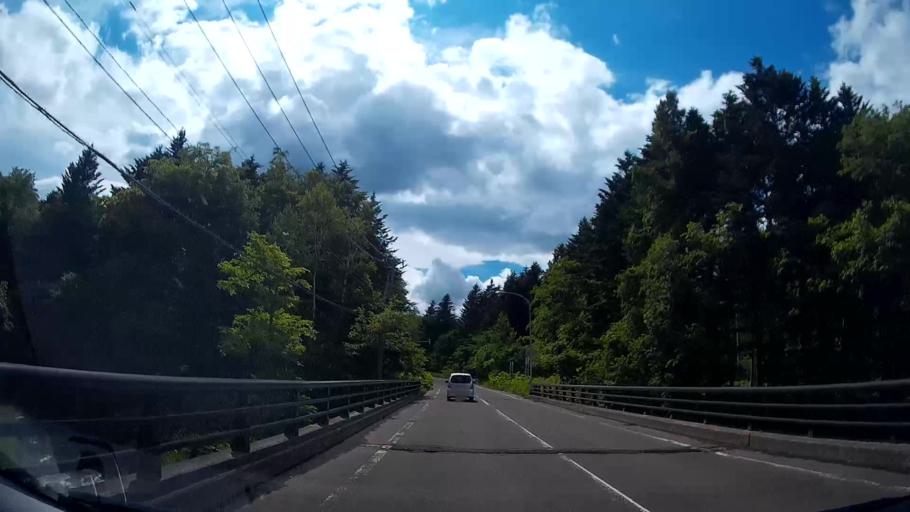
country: JP
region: Hokkaido
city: Kitahiroshima
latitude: 42.8434
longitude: 141.4703
